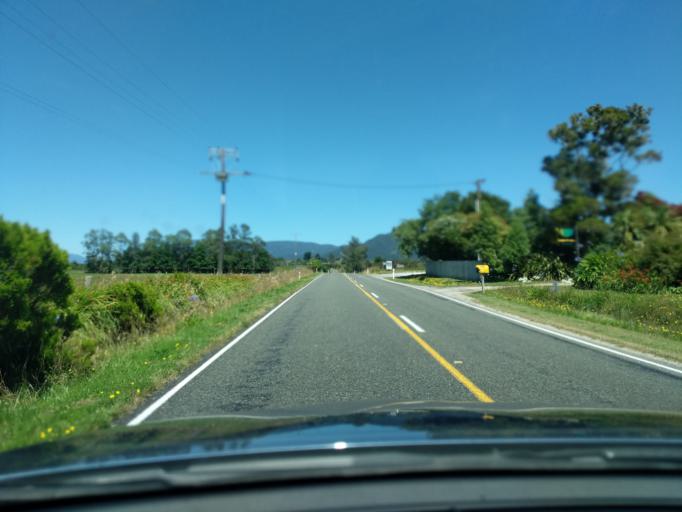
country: NZ
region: Tasman
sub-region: Tasman District
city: Takaka
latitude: -40.6852
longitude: 172.6565
